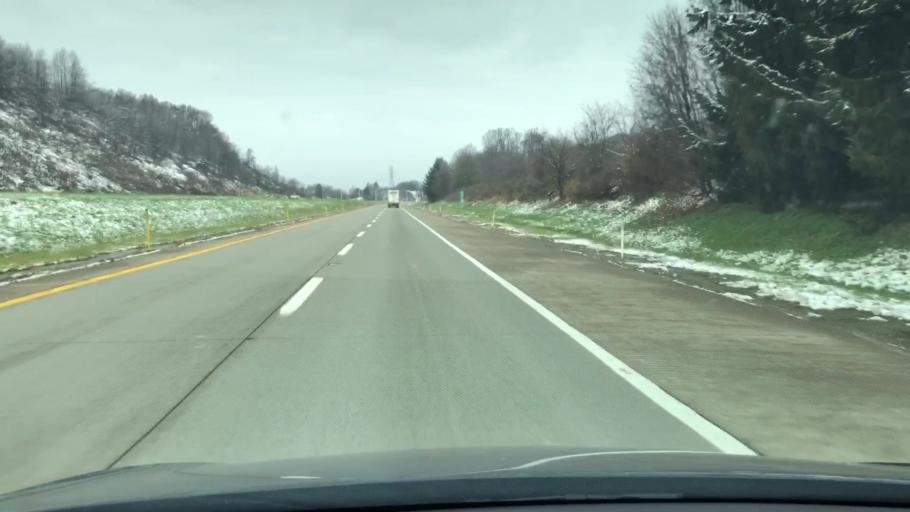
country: US
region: Pennsylvania
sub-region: Westmoreland County
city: Delmont
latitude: 40.3759
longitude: -79.5617
